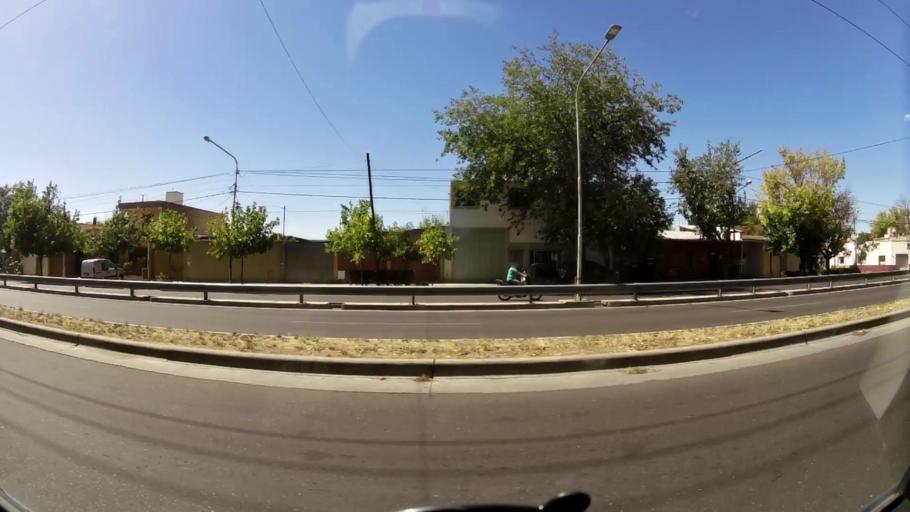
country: AR
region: Mendoza
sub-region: Departamento de Godoy Cruz
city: Godoy Cruz
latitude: -32.9160
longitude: -68.8640
